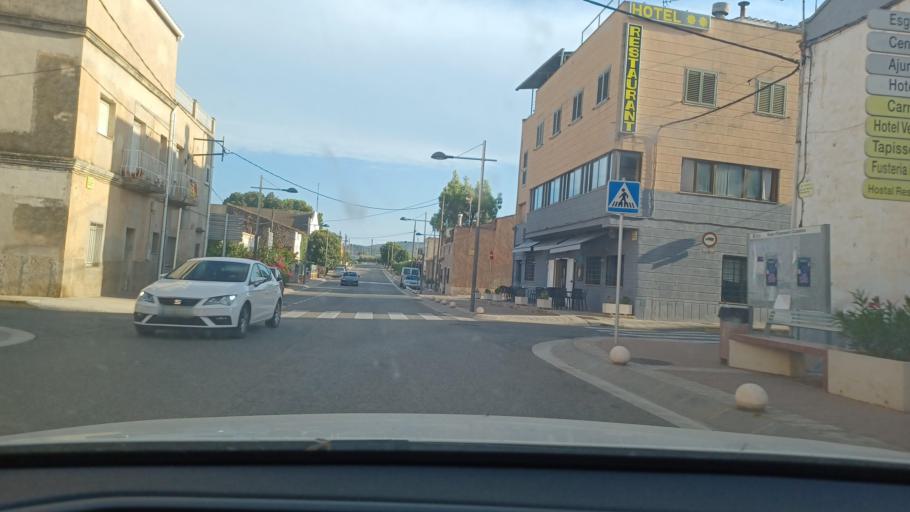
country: ES
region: Catalonia
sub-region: Provincia de Tarragona
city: Santa Barbara
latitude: 40.7153
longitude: 0.5018
